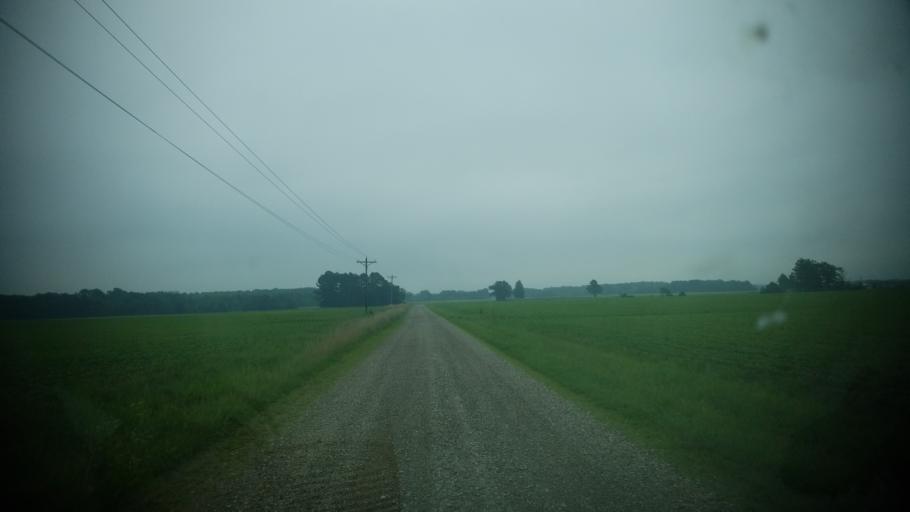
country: US
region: Illinois
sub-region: Clay County
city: Flora
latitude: 38.5881
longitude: -88.3710
